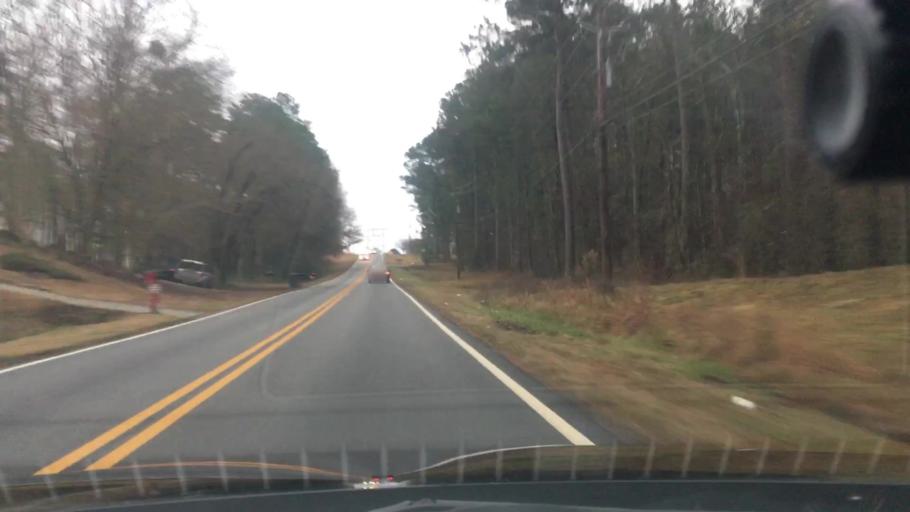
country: US
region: Georgia
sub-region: Bibb County
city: Macon
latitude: 32.9199
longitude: -83.7237
